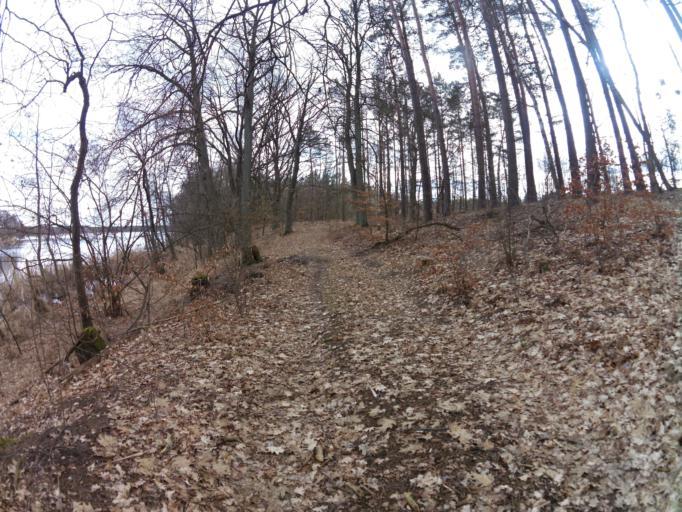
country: PL
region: Lubusz
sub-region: Powiat gorzowski
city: Lubiszyn
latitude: 52.7918
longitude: 14.8353
